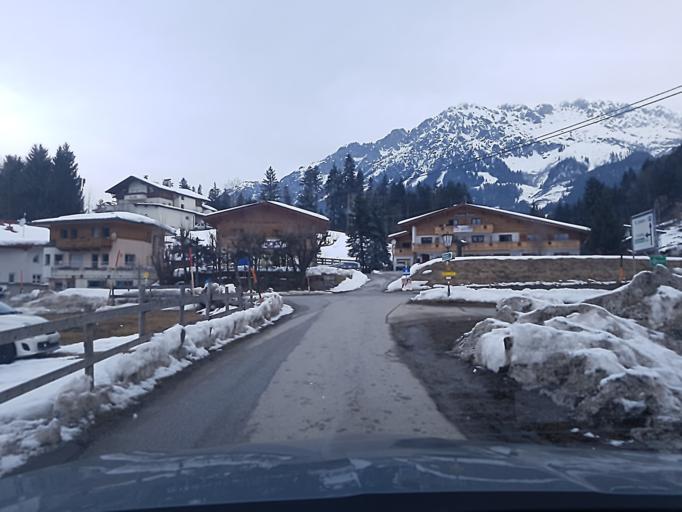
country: AT
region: Tyrol
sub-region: Politischer Bezirk Kufstein
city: Scheffau am Wilden Kaiser
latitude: 47.5213
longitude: 12.2530
